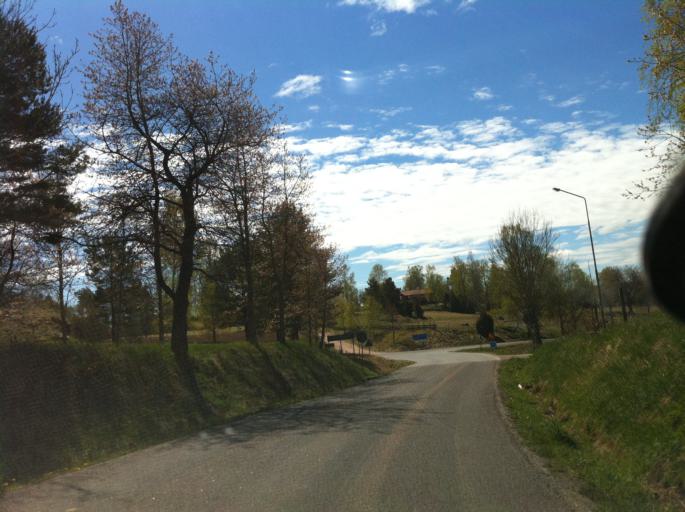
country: SE
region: Kalmar
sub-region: Vimmerby Kommun
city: Sodra Vi
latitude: 57.7810
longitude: 15.8632
